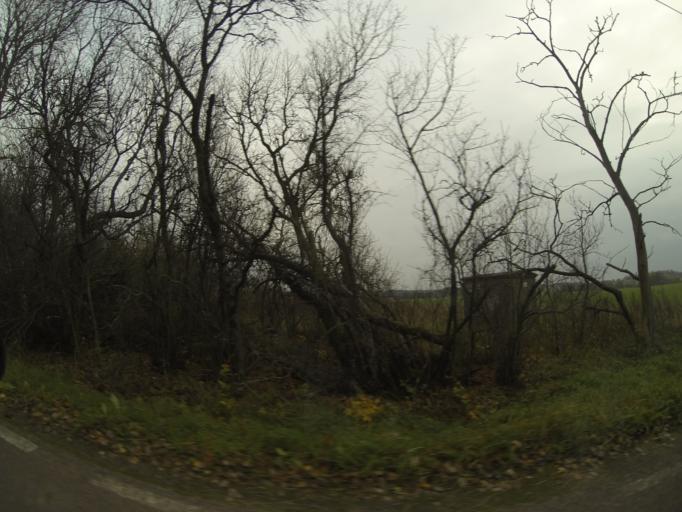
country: SE
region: Vaestmanland
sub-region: Vasteras
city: Skultuna
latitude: 59.6604
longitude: 16.4597
